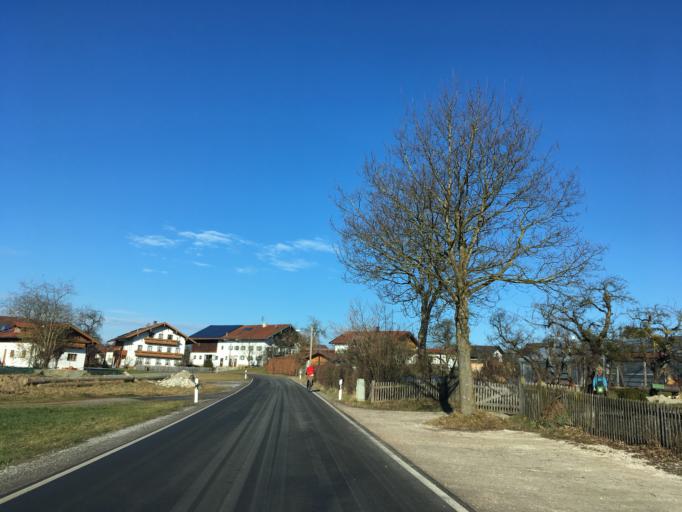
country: DE
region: Bavaria
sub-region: Upper Bavaria
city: Riedering
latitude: 47.8250
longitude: 12.2167
